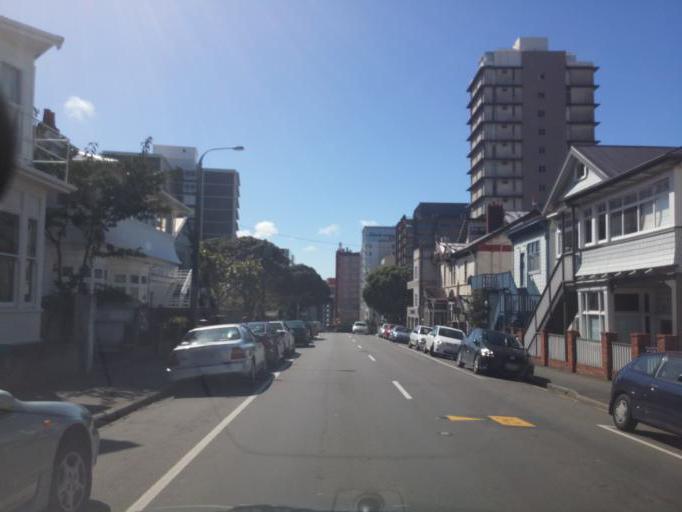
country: NZ
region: Wellington
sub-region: Wellington City
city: Wellington
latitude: -41.2872
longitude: 174.7728
